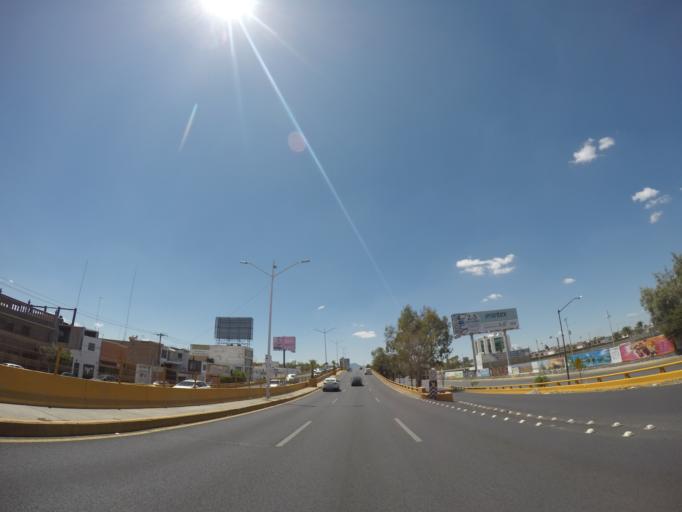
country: MX
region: San Luis Potosi
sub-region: San Luis Potosi
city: San Luis Potosi
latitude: 22.1328
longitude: -100.9871
